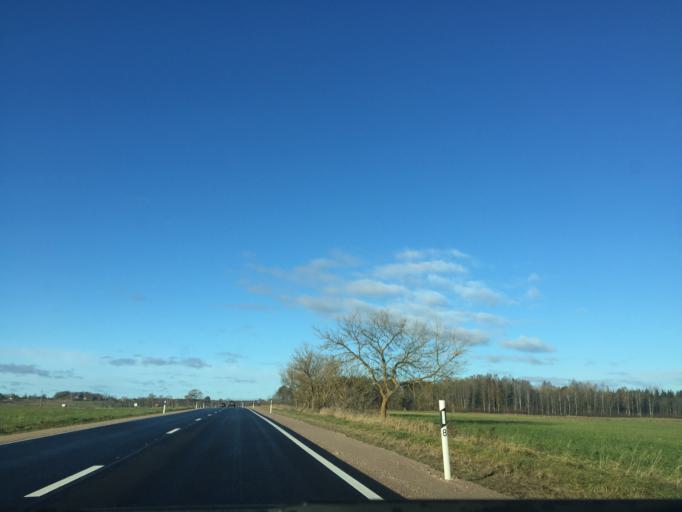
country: LV
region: Engure
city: Smarde
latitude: 56.9209
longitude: 23.2954
